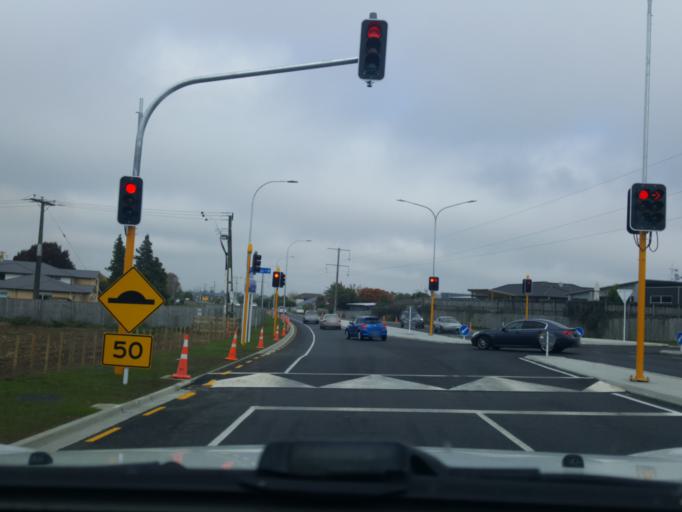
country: NZ
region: Waikato
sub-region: Hamilton City
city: Hamilton
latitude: -37.7321
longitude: 175.2873
